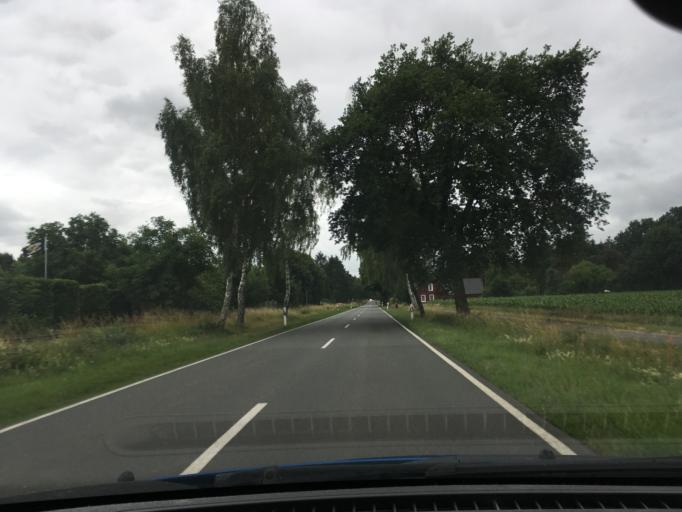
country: DE
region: Lower Saxony
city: Wulfsen
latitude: 53.2917
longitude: 10.1433
